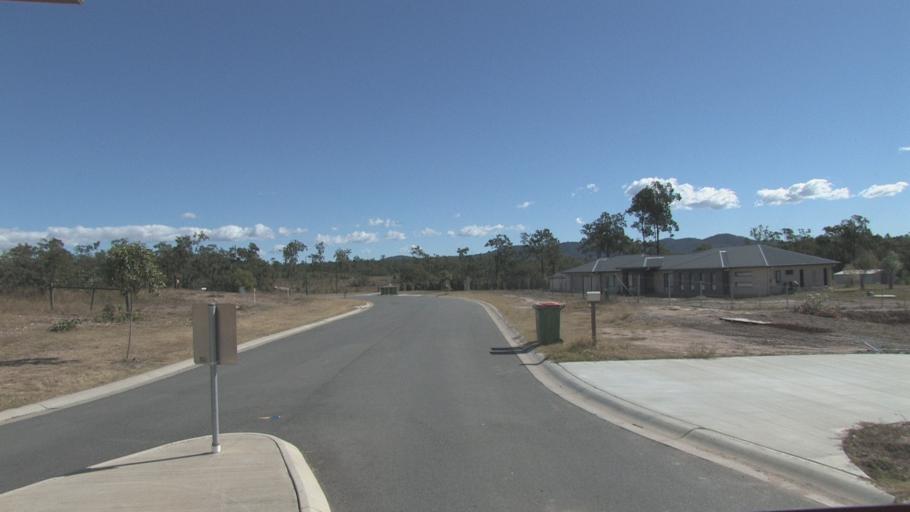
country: AU
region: Queensland
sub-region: Logan
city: North Maclean
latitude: -27.7598
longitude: 152.9327
